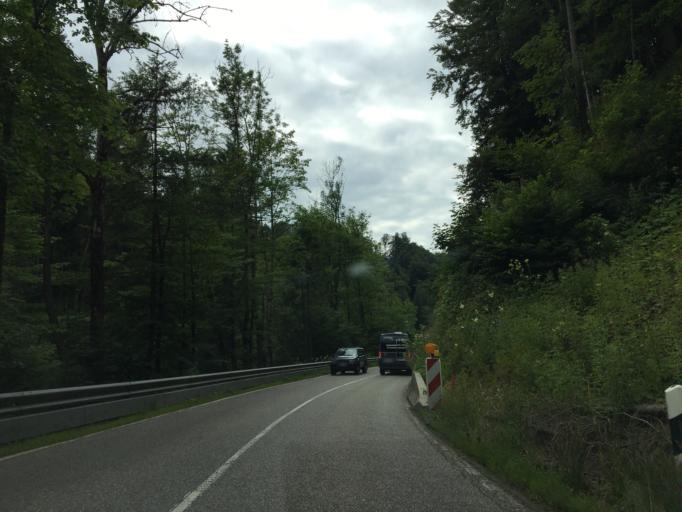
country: DE
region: Bavaria
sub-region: Upper Bavaria
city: Miesbach
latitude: 47.7790
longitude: 11.8776
